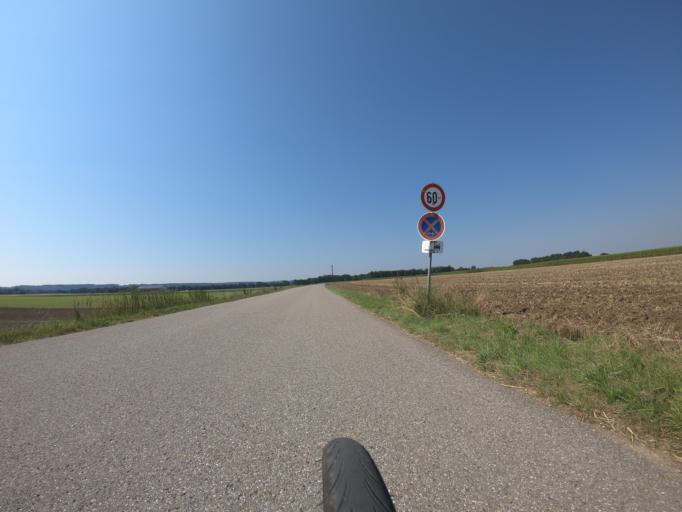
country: DE
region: Bavaria
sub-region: Upper Bavaria
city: Emmering
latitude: 48.2038
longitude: 11.2901
